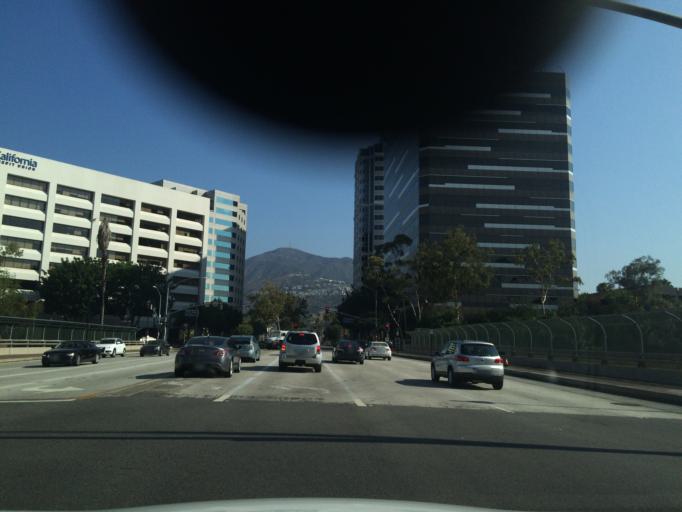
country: US
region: California
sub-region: Los Angeles County
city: North Glendale
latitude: 34.1559
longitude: -118.2550
